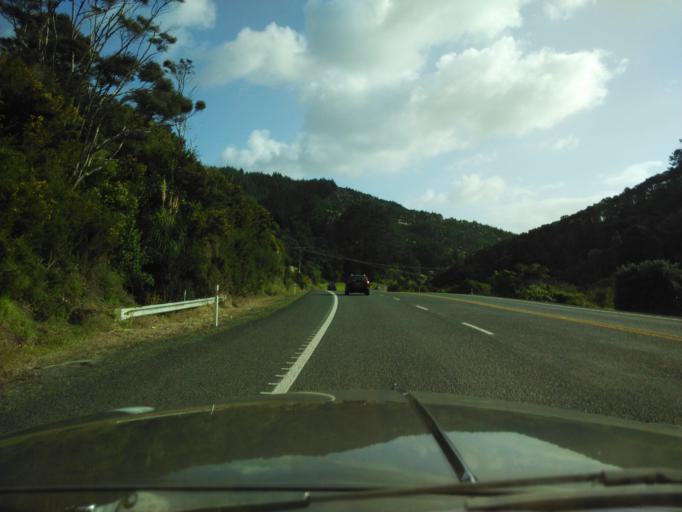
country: NZ
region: Auckland
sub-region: Auckland
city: Wellsford
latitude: -36.3437
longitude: 174.5639
